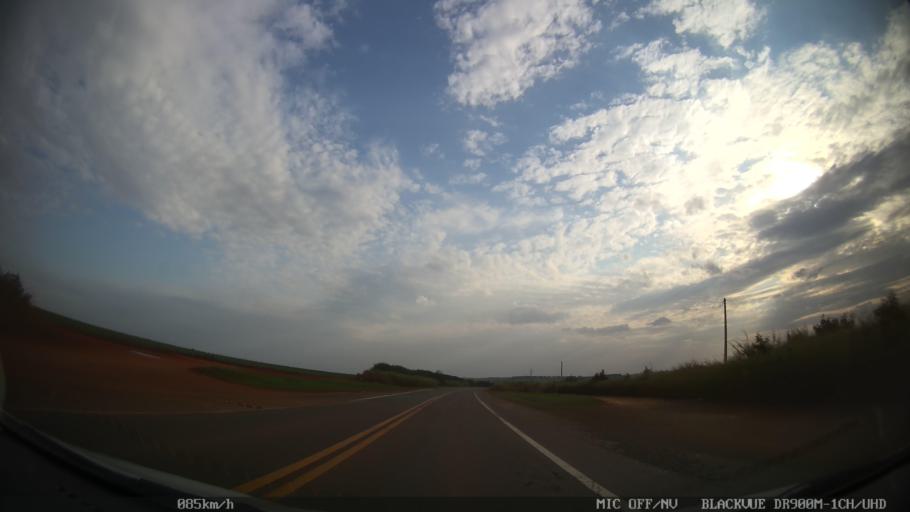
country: BR
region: Sao Paulo
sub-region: Cosmopolis
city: Cosmopolis
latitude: -22.6265
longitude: -47.2625
